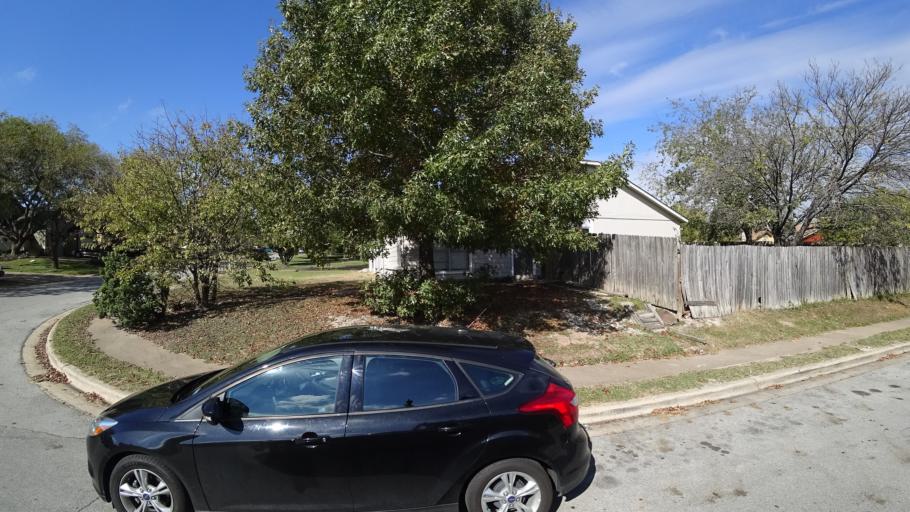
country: US
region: Texas
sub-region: Travis County
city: Windemere
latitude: 30.4536
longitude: -97.6487
